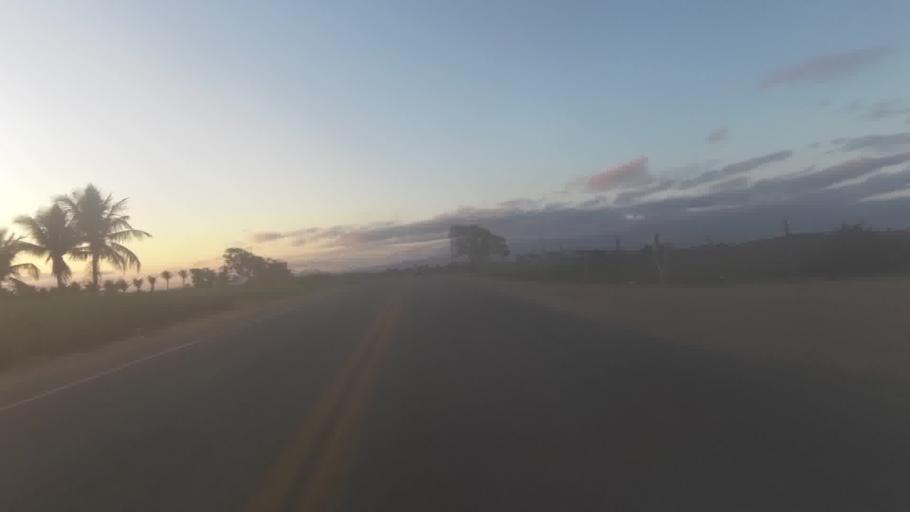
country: BR
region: Espirito Santo
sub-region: Marataizes
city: Marataizes
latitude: -21.0788
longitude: -40.8496
